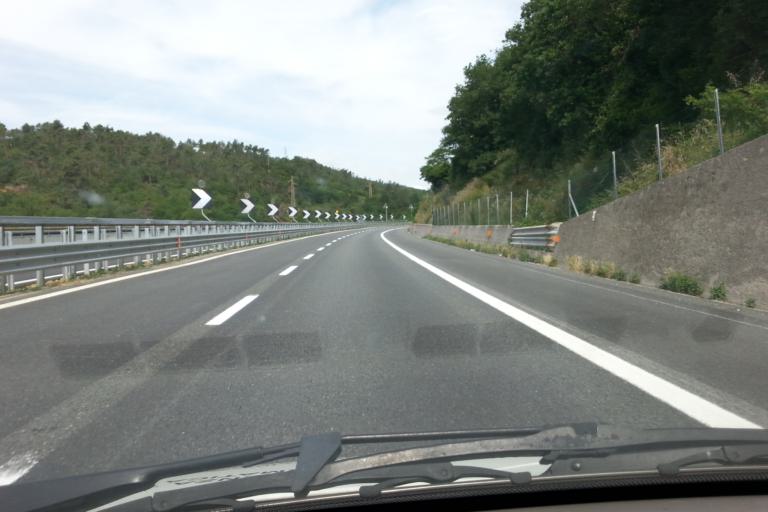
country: IT
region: Liguria
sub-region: Provincia di Savona
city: Valleggia
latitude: 44.2922
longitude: 8.4368
